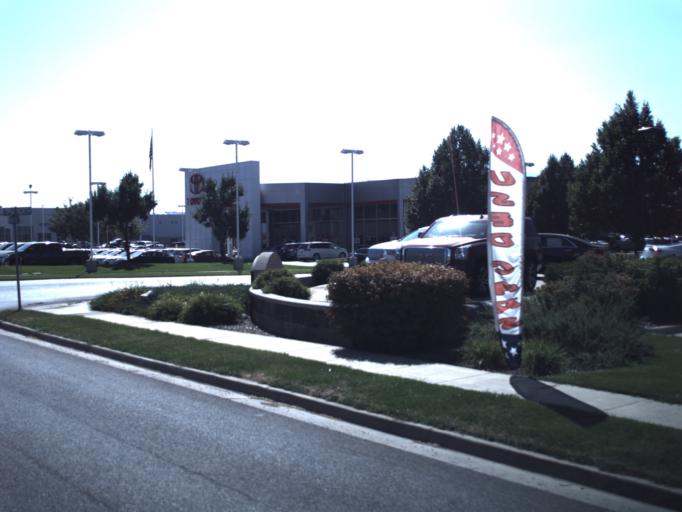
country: US
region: Utah
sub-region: Cache County
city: North Logan
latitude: 41.7682
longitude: -111.8343
